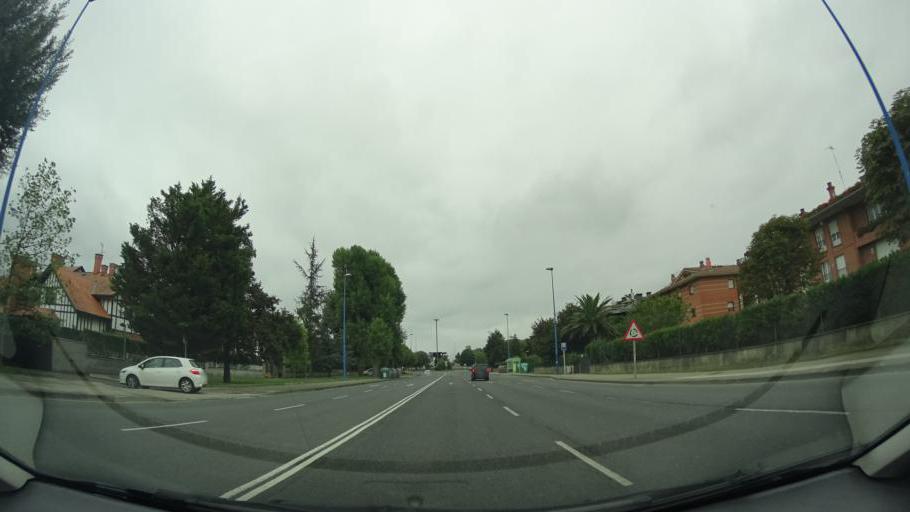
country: ES
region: Basque Country
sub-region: Bizkaia
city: Algorta
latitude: 43.3343
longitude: -3.0044
